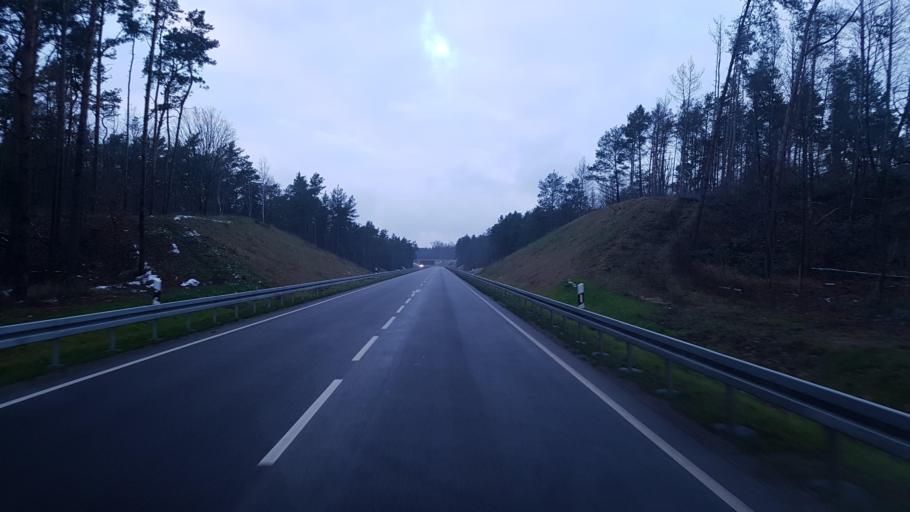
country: DE
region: Brandenburg
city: Wildau
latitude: 52.3172
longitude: 13.6599
